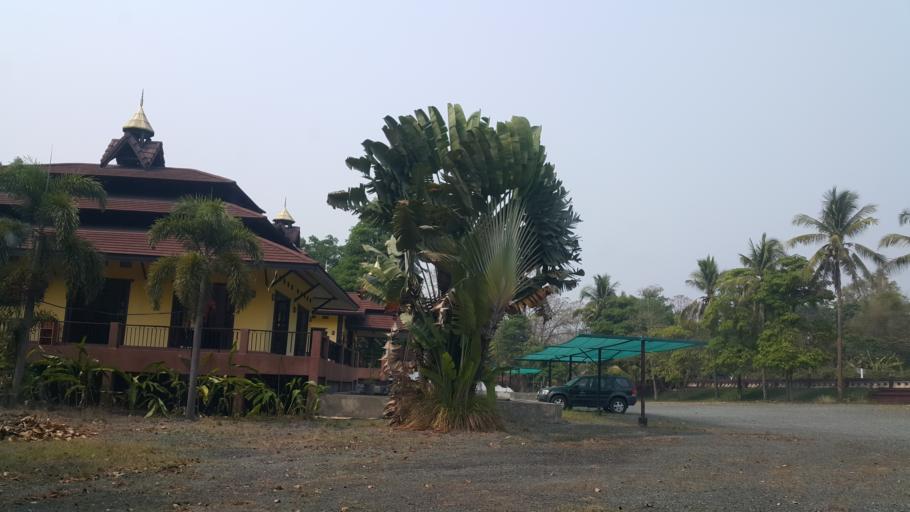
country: TH
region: Chiang Mai
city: Mae On
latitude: 18.8090
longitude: 99.2370
